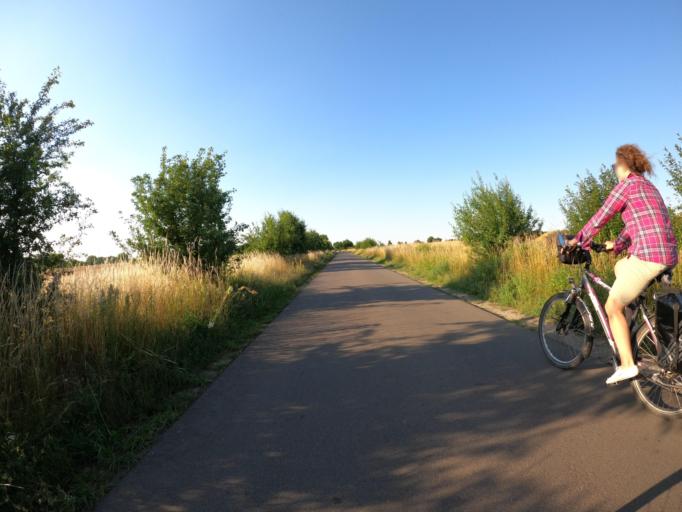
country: DE
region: Brandenburg
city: Tantow
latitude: 53.2742
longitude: 14.3529
